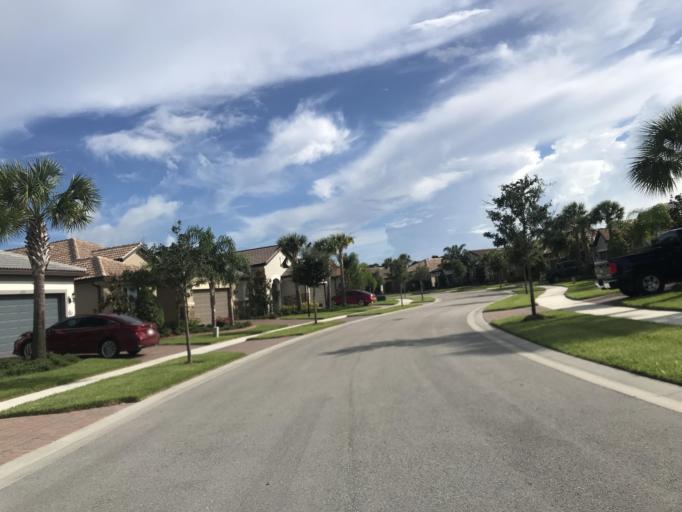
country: US
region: Florida
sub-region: Indian River County
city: Gifford
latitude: 27.6903
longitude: -80.4295
